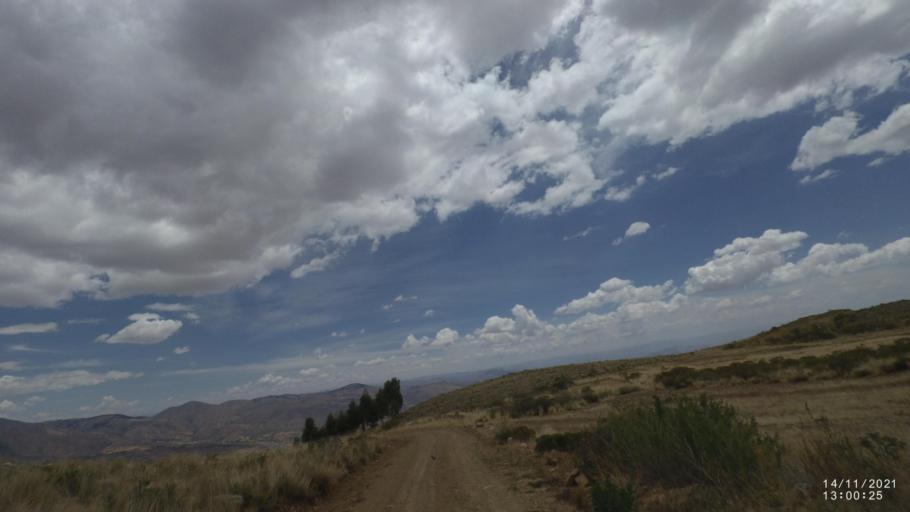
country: BO
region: Cochabamba
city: Colomi
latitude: -17.3639
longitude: -65.9778
